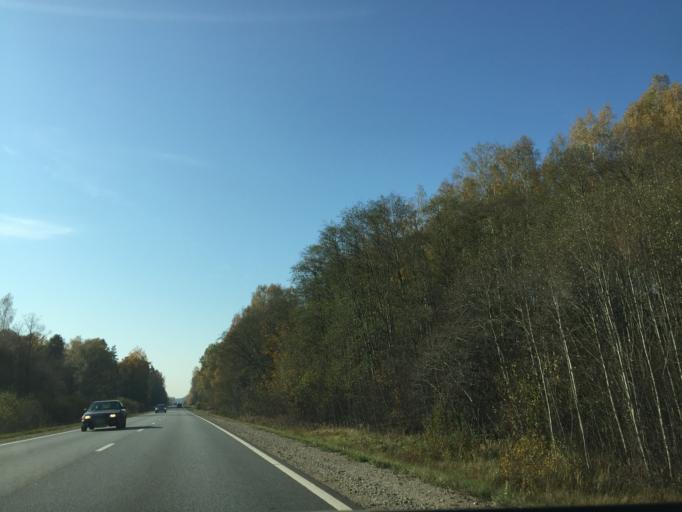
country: LV
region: Jaunpils
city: Jaunpils
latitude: 56.6990
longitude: 23.1518
